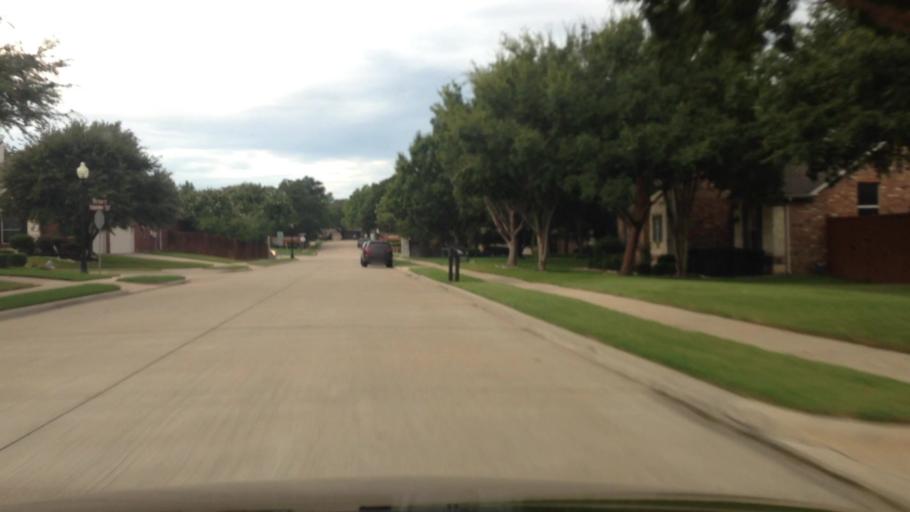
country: US
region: Texas
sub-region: Denton County
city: Flower Mound
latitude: 33.0050
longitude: -97.0437
